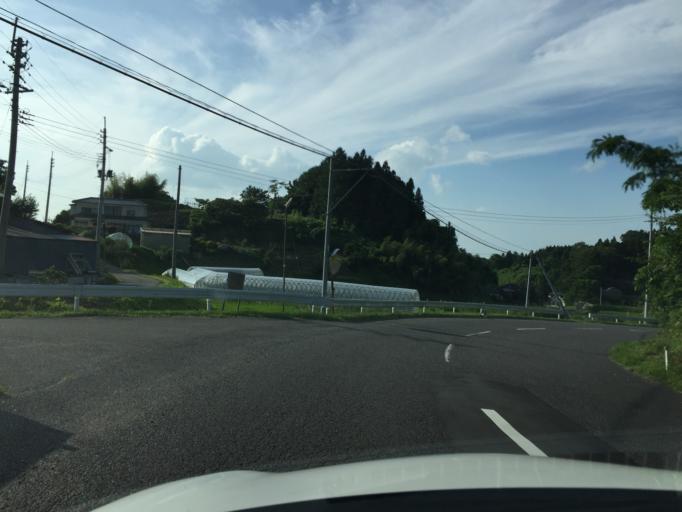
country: JP
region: Fukushima
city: Miharu
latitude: 37.3739
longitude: 140.5128
